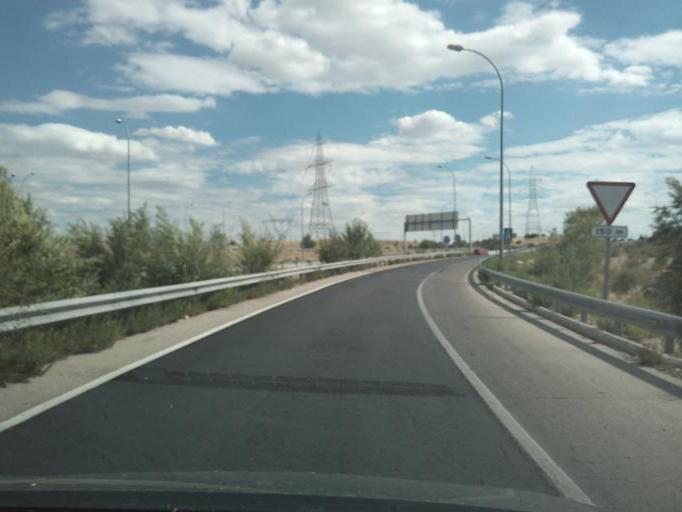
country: ES
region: Madrid
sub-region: Provincia de Madrid
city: San Sebastian de los Reyes
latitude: 40.5532
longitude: -3.6079
